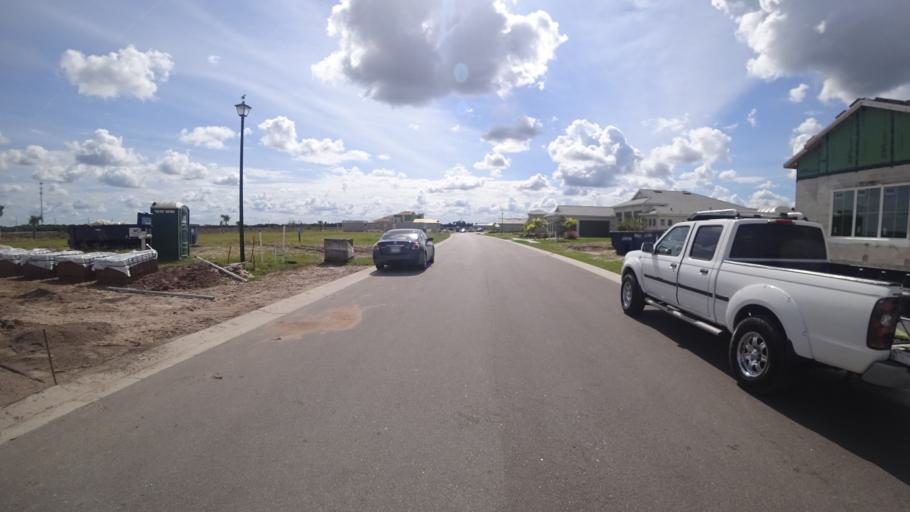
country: US
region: Florida
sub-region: Sarasota County
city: The Meadows
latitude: 27.3921
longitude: -82.3608
